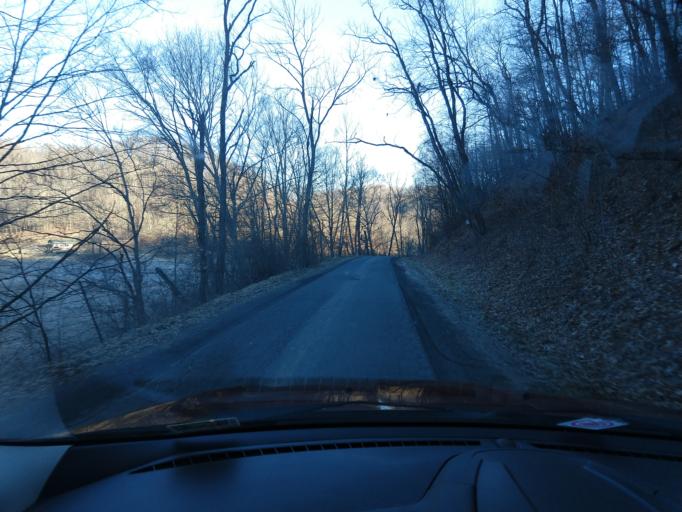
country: US
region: West Virginia
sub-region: Greenbrier County
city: Rainelle
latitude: 37.8926
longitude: -80.7314
